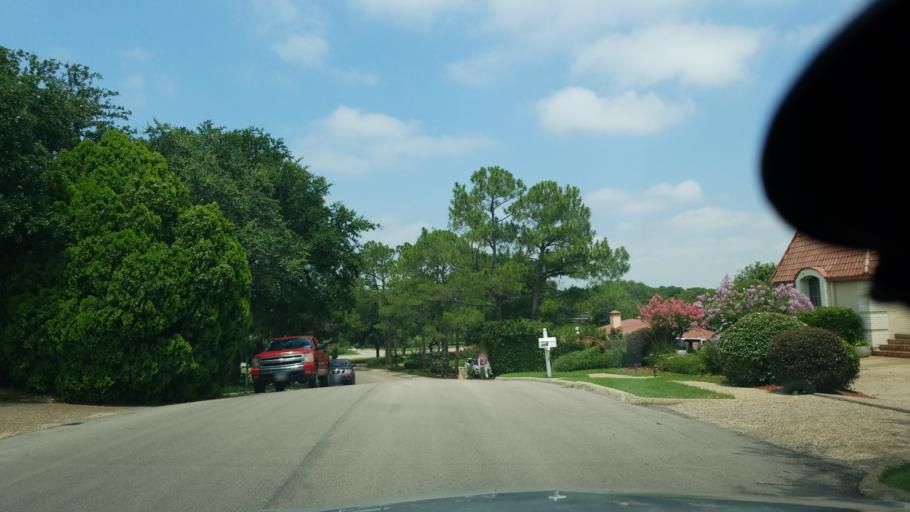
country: US
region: Texas
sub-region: Dallas County
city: Irving
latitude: 32.8578
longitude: -96.9404
